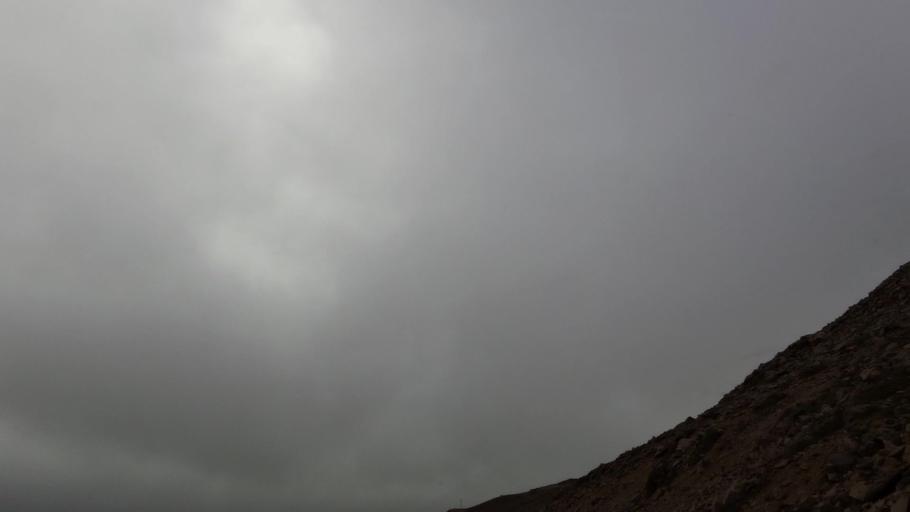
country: IS
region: West
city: Olafsvik
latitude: 65.5270
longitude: -24.4248
